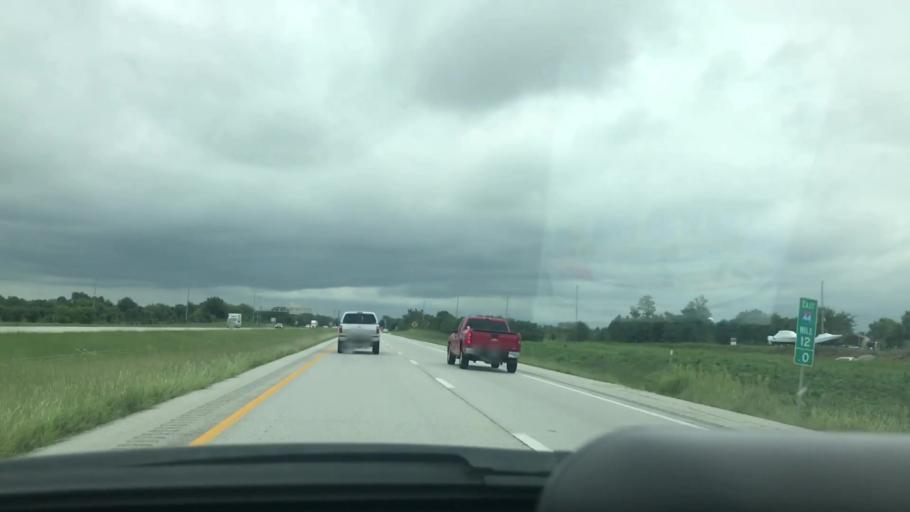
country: US
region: Missouri
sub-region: Jasper County
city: Duenweg
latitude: 37.0620
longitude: -94.4250
